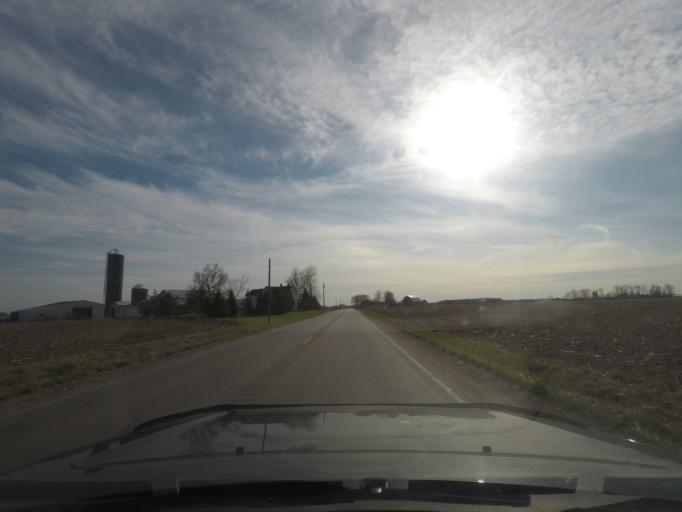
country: US
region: Indiana
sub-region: Elkhart County
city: Wakarusa
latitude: 41.5204
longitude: -85.9698
